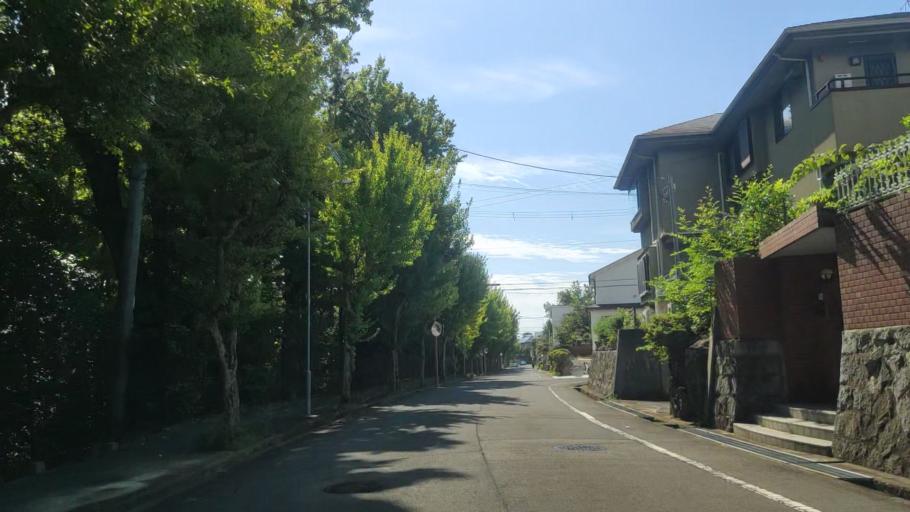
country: JP
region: Osaka
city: Mino
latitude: 34.8241
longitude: 135.5150
